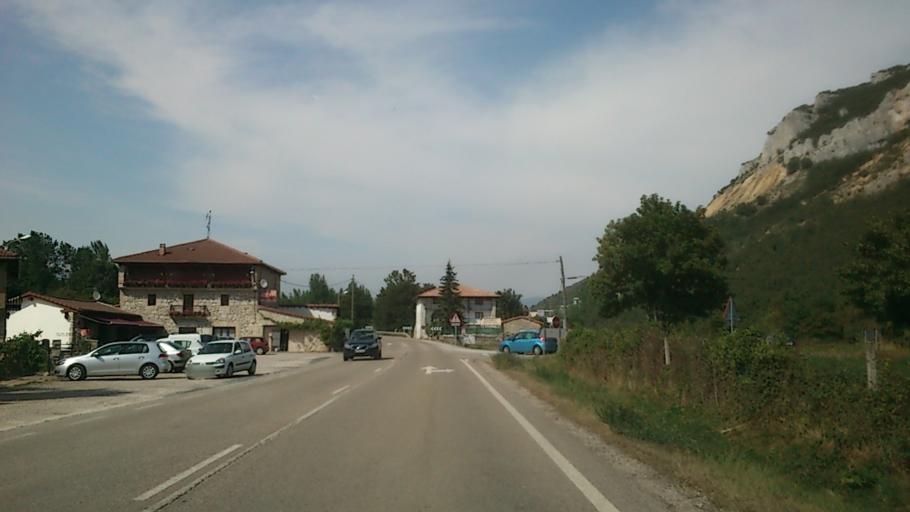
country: ES
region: Castille and Leon
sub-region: Provincia de Burgos
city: Espinosa de los Monteros
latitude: 43.0363
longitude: -3.4823
